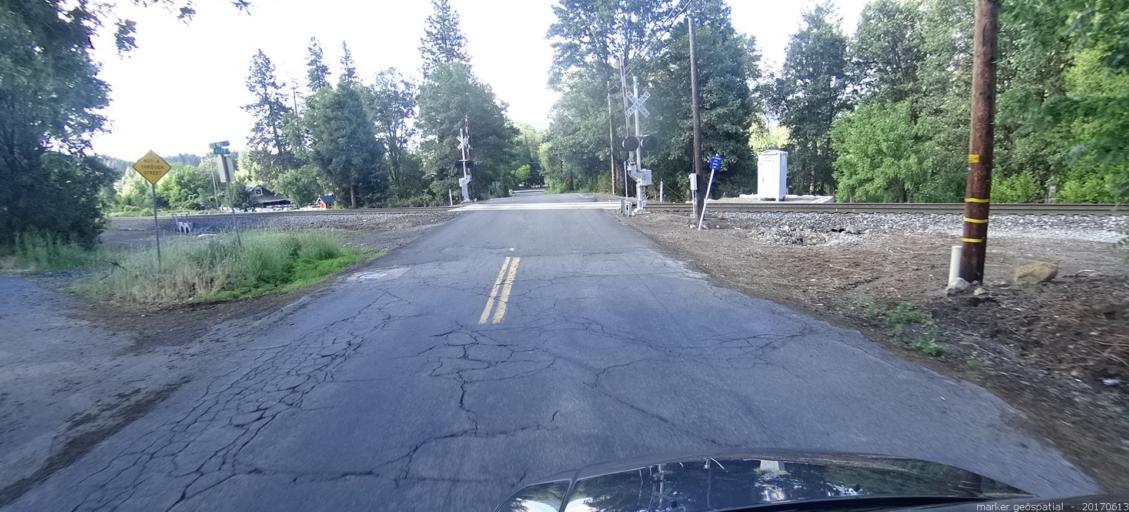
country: US
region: California
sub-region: Siskiyou County
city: Mount Shasta
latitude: 41.3026
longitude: -122.3112
